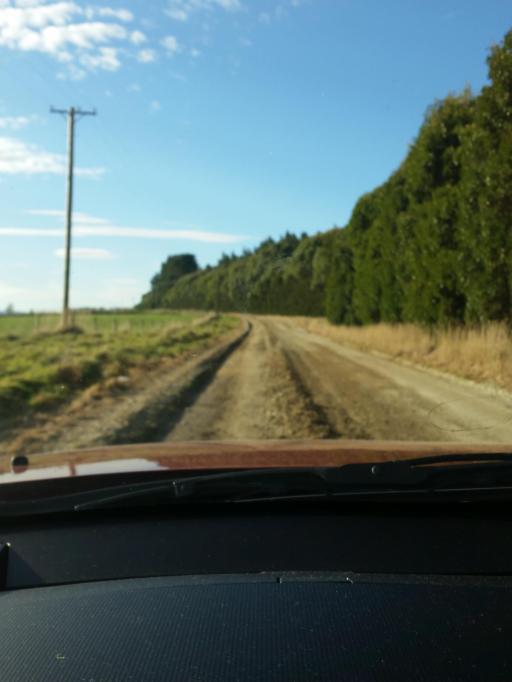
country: NZ
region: Southland
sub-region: Gore District
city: Gore
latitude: -46.2541
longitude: 168.7473
